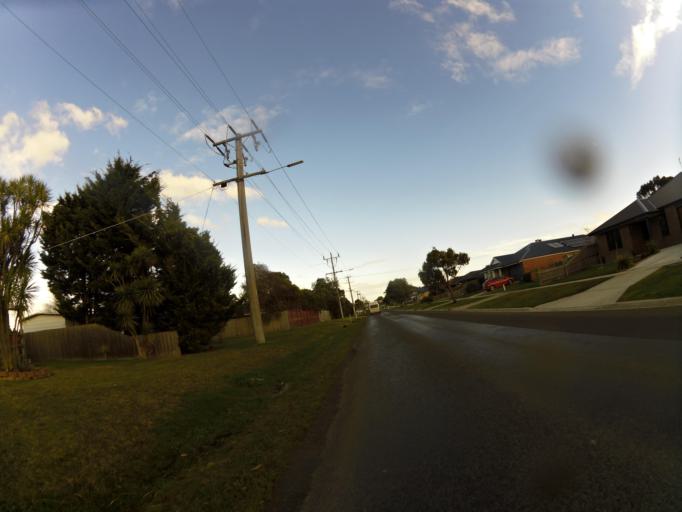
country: AU
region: Victoria
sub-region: Bass Coast
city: North Wonthaggi
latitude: -38.5597
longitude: 145.5482
